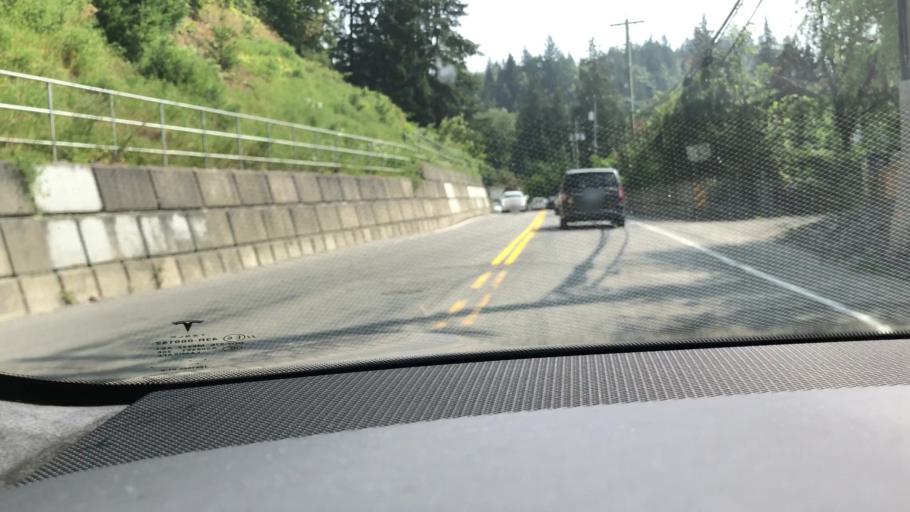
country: CA
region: British Columbia
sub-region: Fraser Valley Regional District
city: Chilliwack
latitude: 49.0943
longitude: -121.9721
